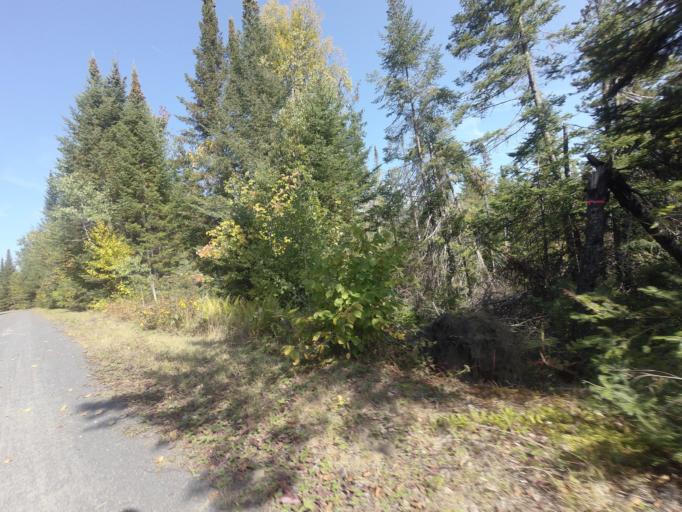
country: CA
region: Quebec
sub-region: Laurentides
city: Sainte-Agathe-des-Monts
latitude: 46.0864
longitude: -74.3408
